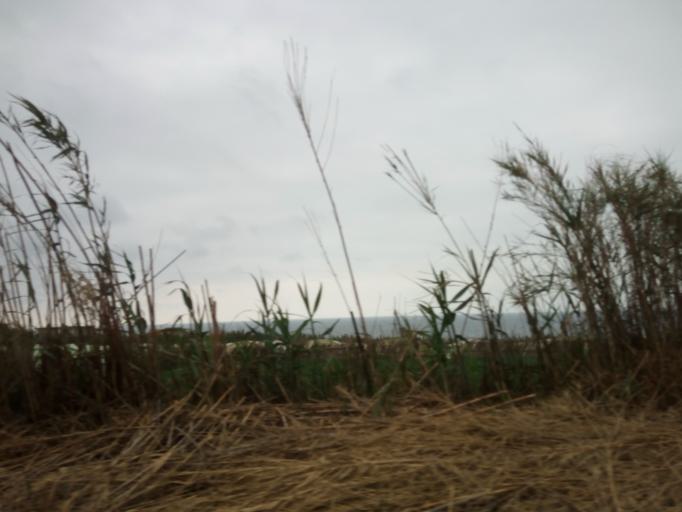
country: DZ
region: Tipaza
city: Tipasa
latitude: 36.5896
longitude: 2.5420
